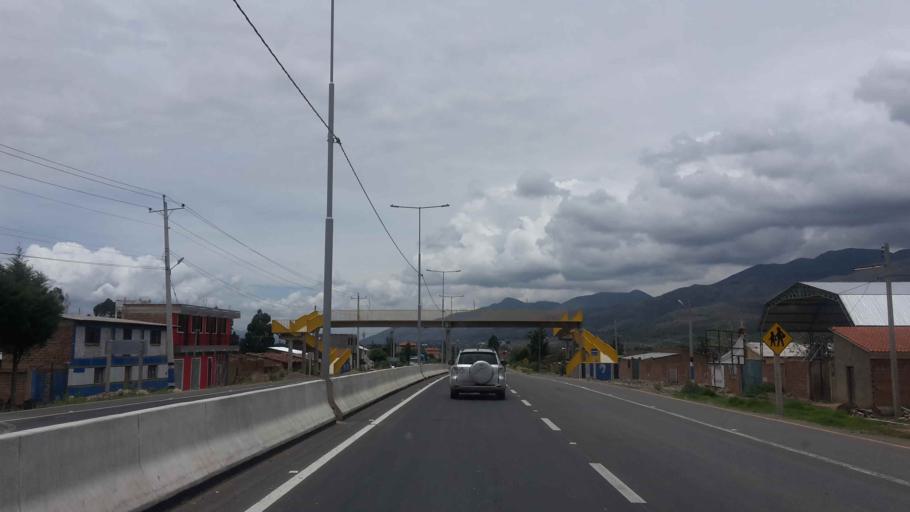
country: BO
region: Cochabamba
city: Punata
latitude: -17.5147
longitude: -65.8331
